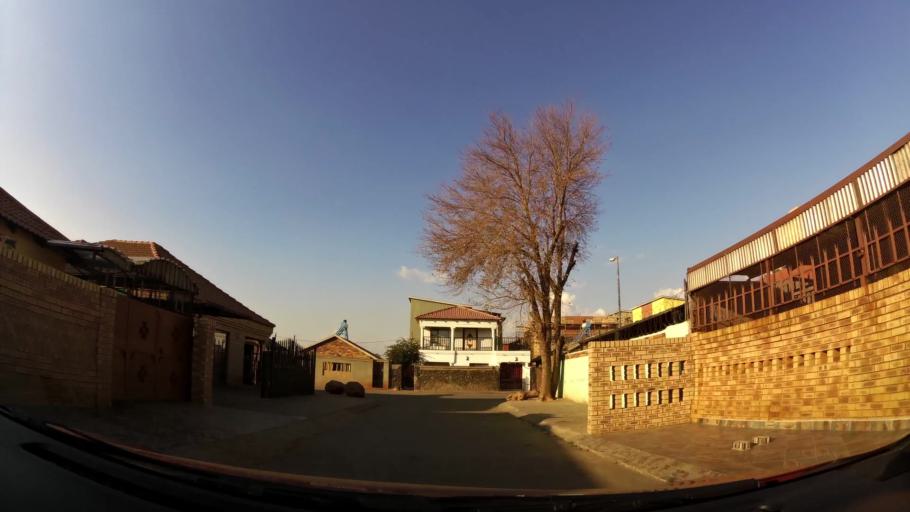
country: ZA
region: Gauteng
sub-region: City of Johannesburg Metropolitan Municipality
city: Soweto
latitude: -26.2282
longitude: 27.8540
